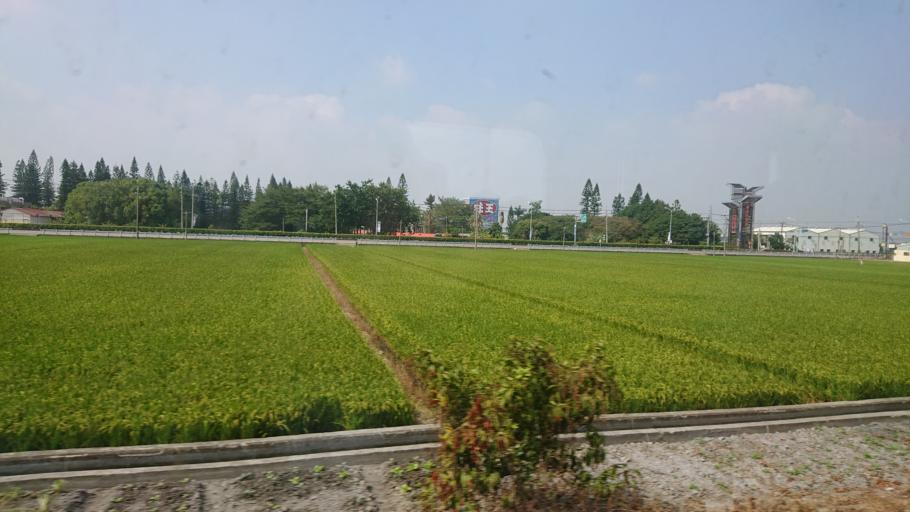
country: TW
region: Taiwan
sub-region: Yunlin
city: Douliu
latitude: 23.6415
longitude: 120.4712
